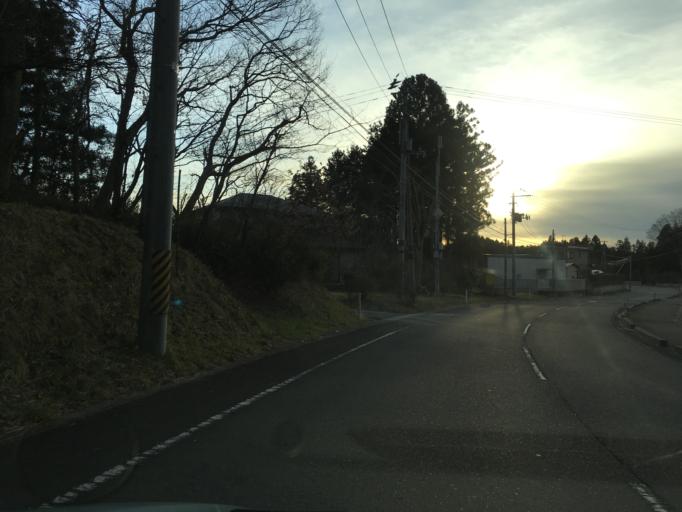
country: JP
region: Miyagi
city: Wakuya
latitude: 38.7023
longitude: 141.1156
